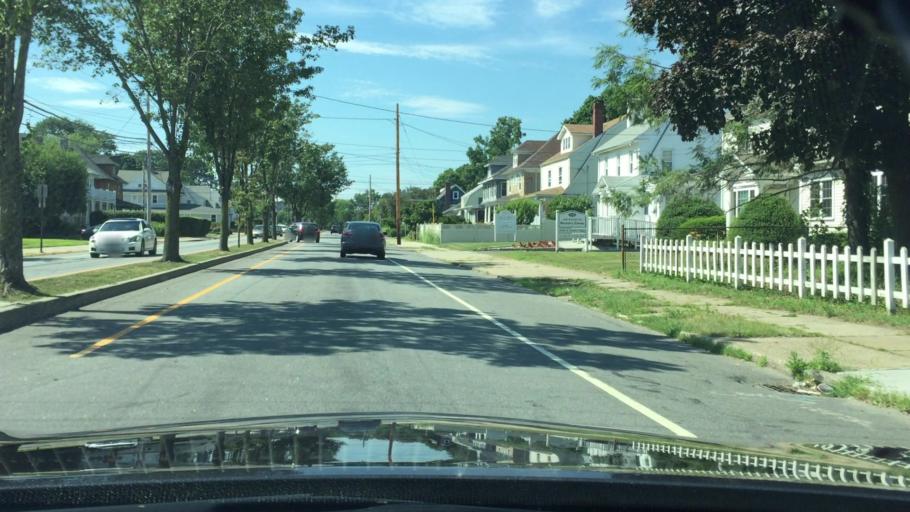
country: US
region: Connecticut
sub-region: Fairfield County
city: Trumbull
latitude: 41.2065
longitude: -73.2064
